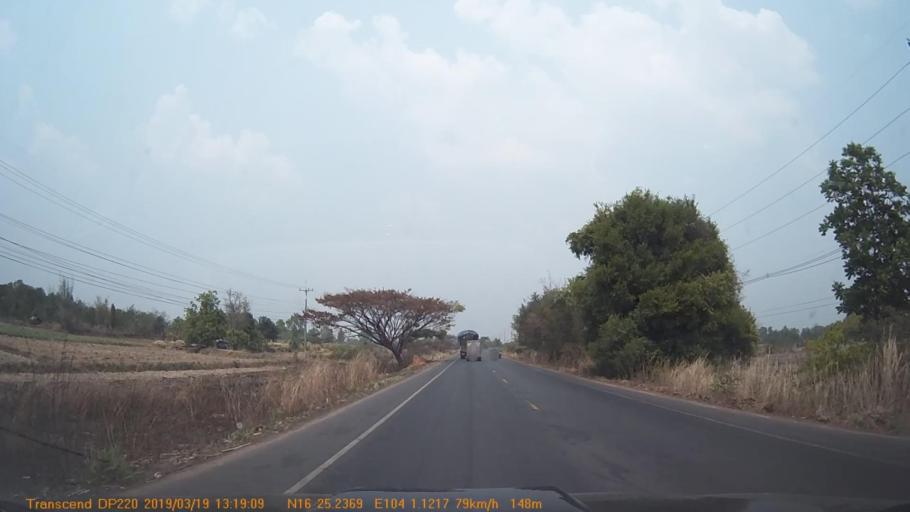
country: TH
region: Kalasin
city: Kuchinarai
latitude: 16.4211
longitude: 104.0189
